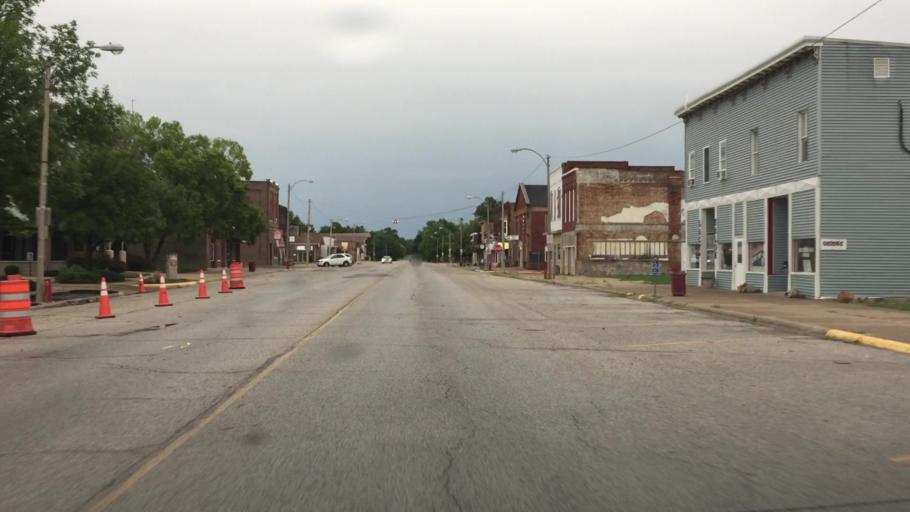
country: US
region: Illinois
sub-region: Hancock County
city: Hamilton
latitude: 40.3931
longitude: -91.3462
